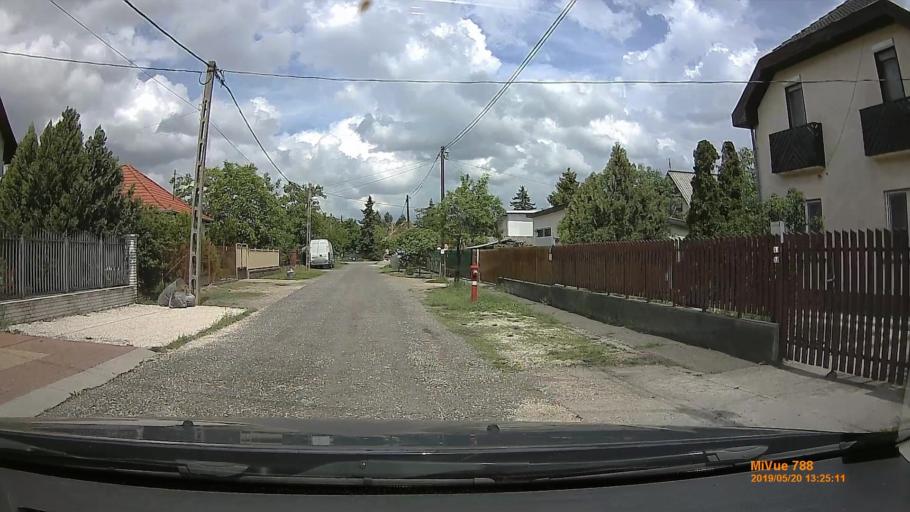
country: HU
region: Budapest
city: Budapest XVII. keruelet
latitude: 47.4687
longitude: 19.2515
